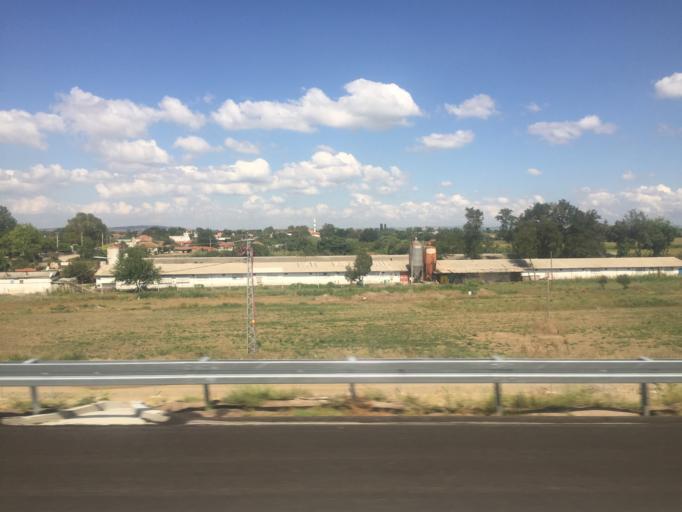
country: TR
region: Balikesir
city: Gobel
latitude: 40.0582
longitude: 28.2385
